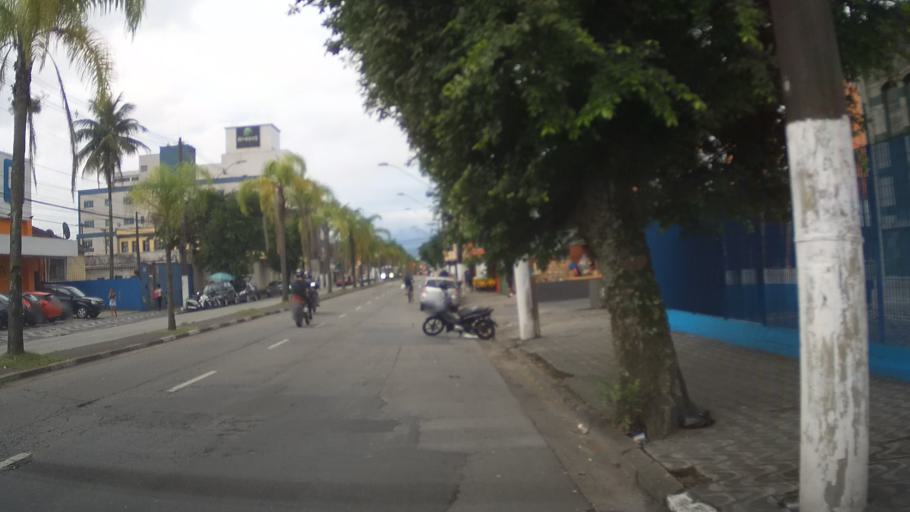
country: BR
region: Sao Paulo
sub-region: Santos
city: Santos
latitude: -23.9431
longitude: -46.3214
